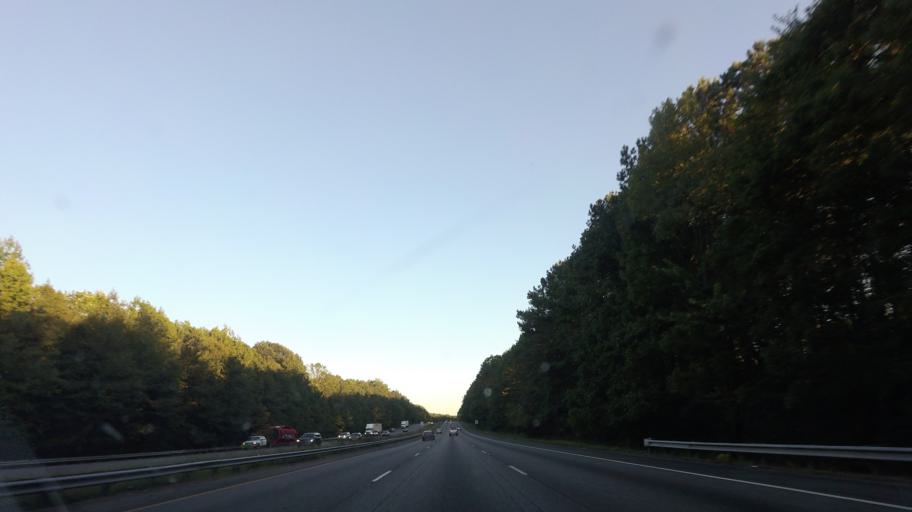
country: US
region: Georgia
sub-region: Monroe County
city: Forsyth
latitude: 33.1319
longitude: -84.0142
